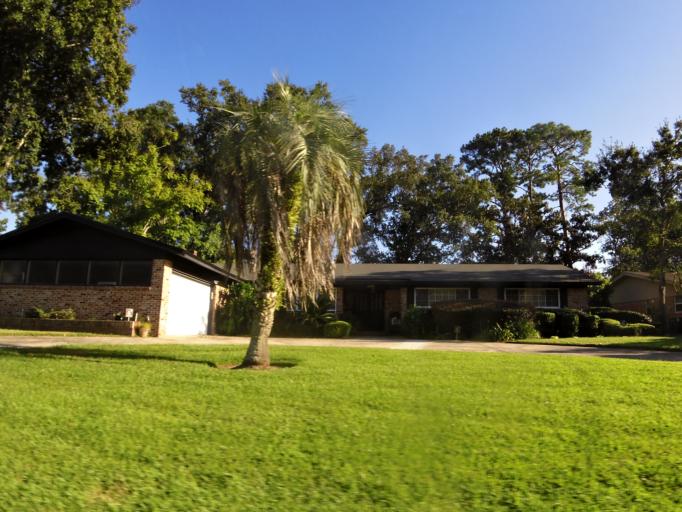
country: US
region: Florida
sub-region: Duval County
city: Jacksonville
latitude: 30.2541
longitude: -81.6354
